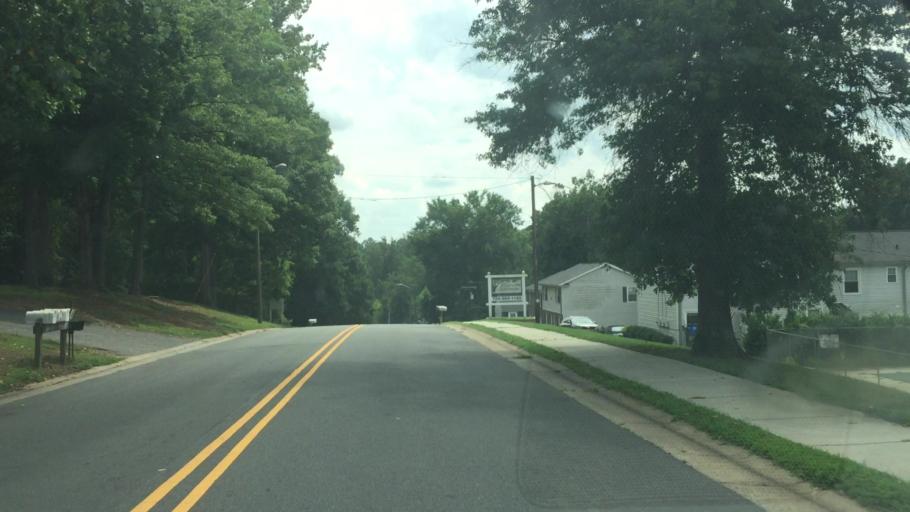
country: US
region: North Carolina
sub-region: Iredell County
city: Mooresville
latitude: 35.5540
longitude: -80.8020
